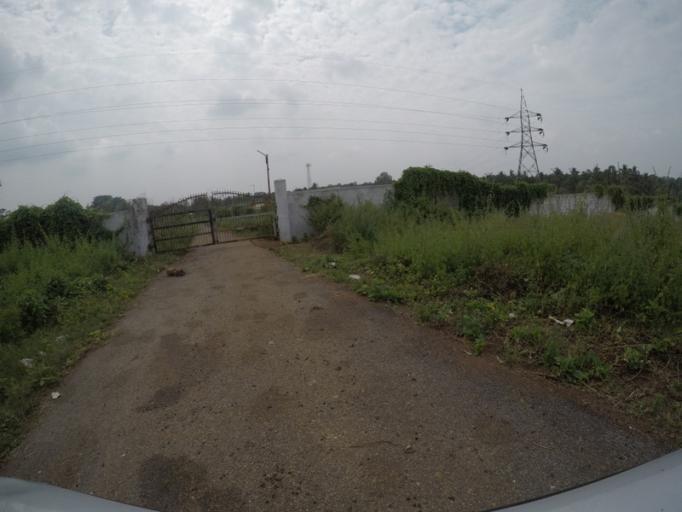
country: IN
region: Karnataka
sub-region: Mandya
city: Malavalli
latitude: 12.4132
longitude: 77.2067
